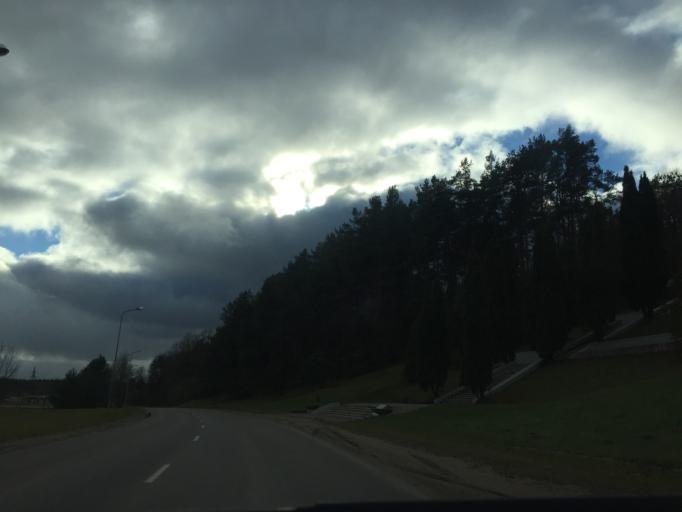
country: LV
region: Tukuma Rajons
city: Tukums
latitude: 56.9667
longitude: 23.1377
